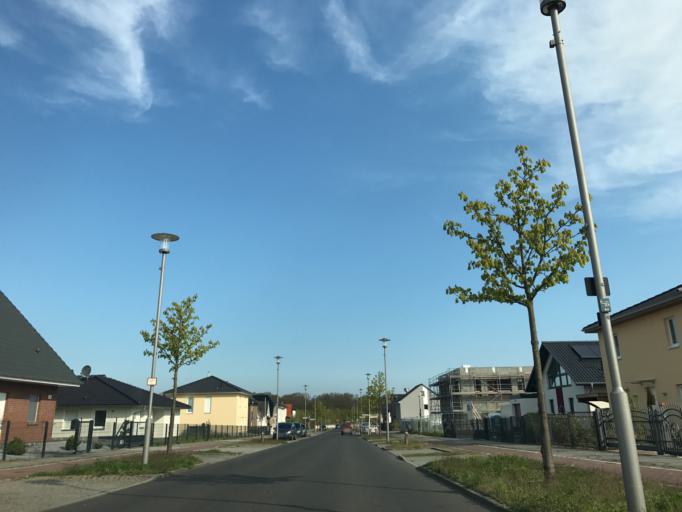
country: DE
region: Berlin
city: Kladow
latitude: 52.4738
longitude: 13.1286
